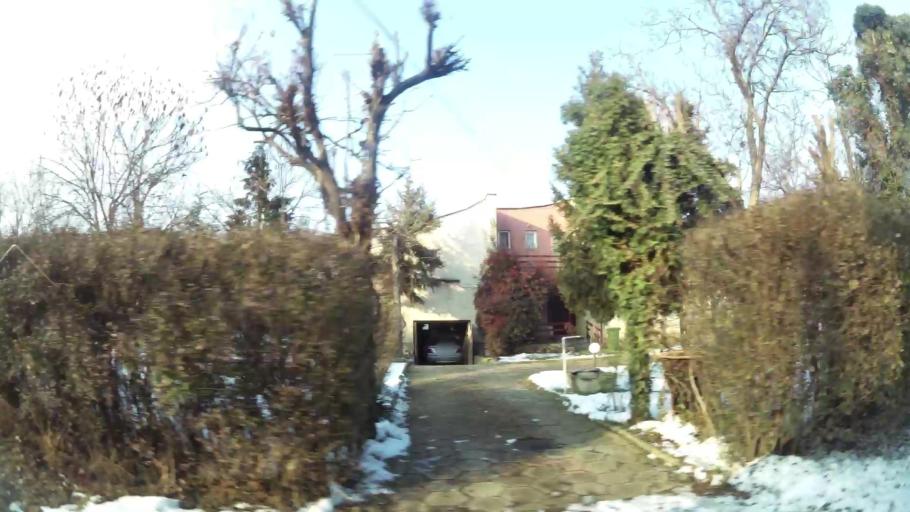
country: MK
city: Creshevo
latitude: 42.0258
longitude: 21.5116
